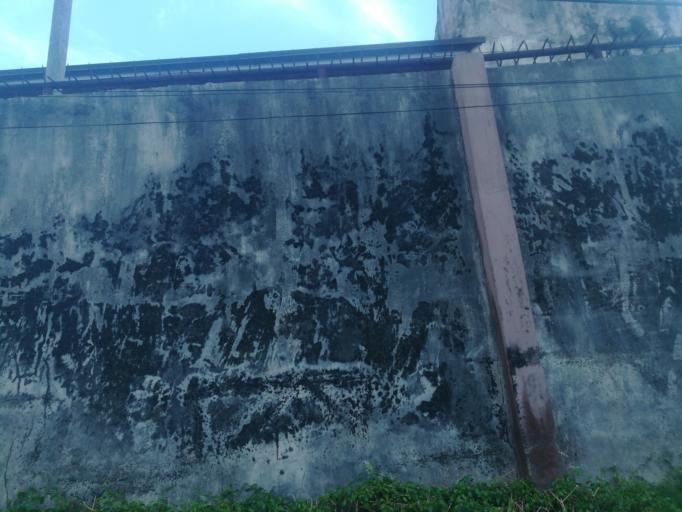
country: NG
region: Lagos
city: Ojota
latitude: 6.5640
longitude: 3.3761
